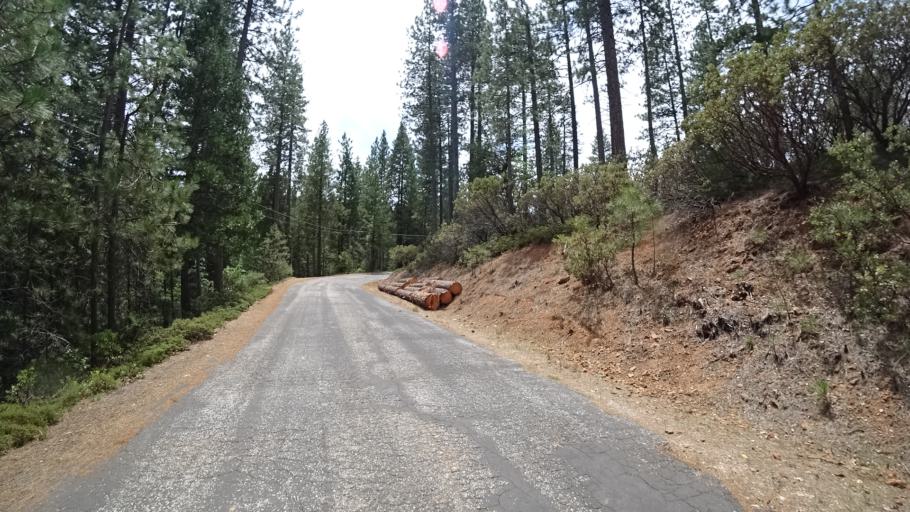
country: US
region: California
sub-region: Calaveras County
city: Arnold
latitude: 38.2347
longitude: -120.3486
